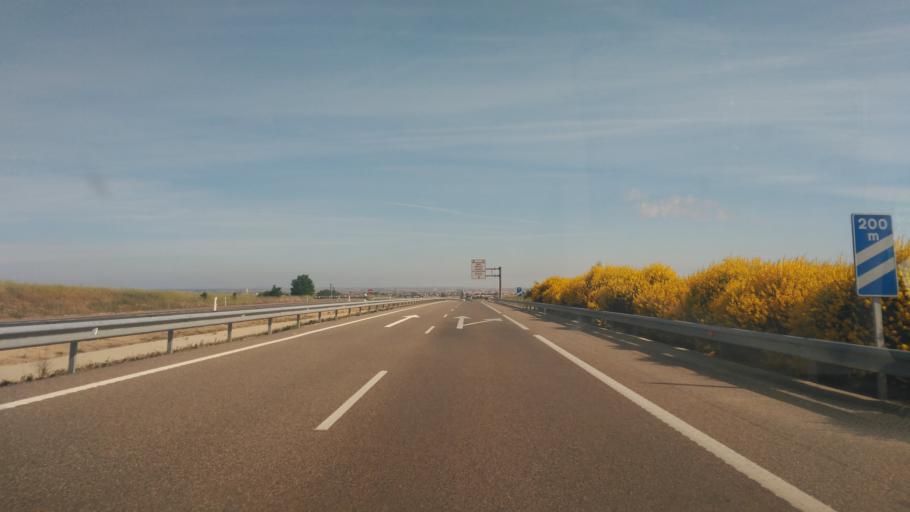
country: ES
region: Castille and Leon
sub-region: Provincia de Zamora
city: Cazurra
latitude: 41.4131
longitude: -5.7205
